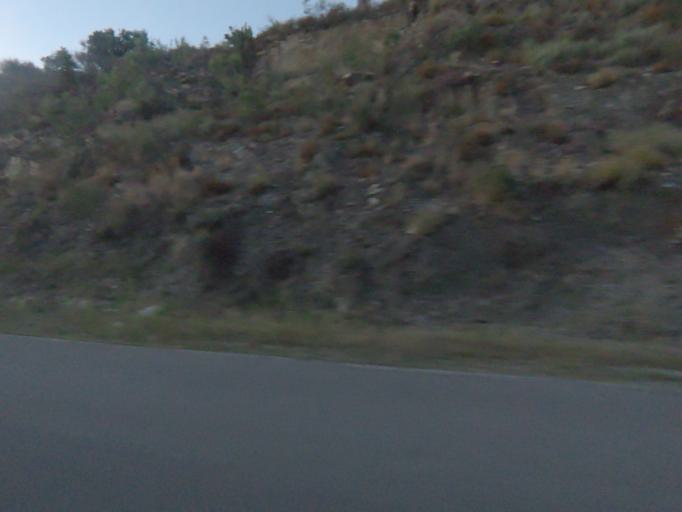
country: PT
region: Viseu
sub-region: Armamar
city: Armamar
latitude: 41.1997
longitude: -7.6966
